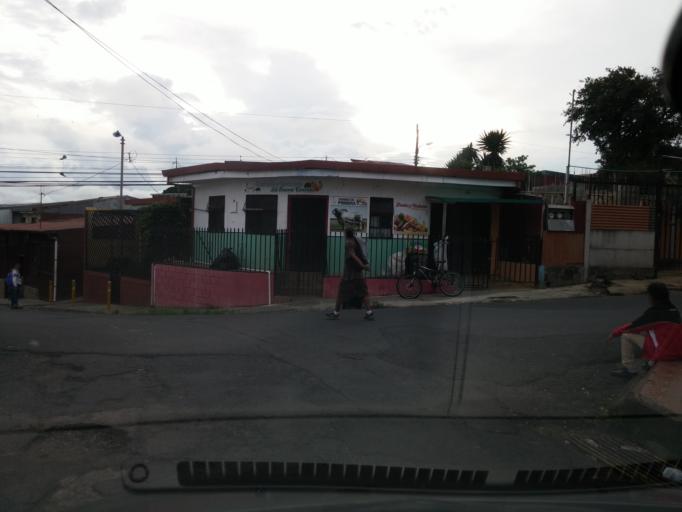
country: CR
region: Heredia
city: Heredia
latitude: 10.0097
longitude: -84.1168
